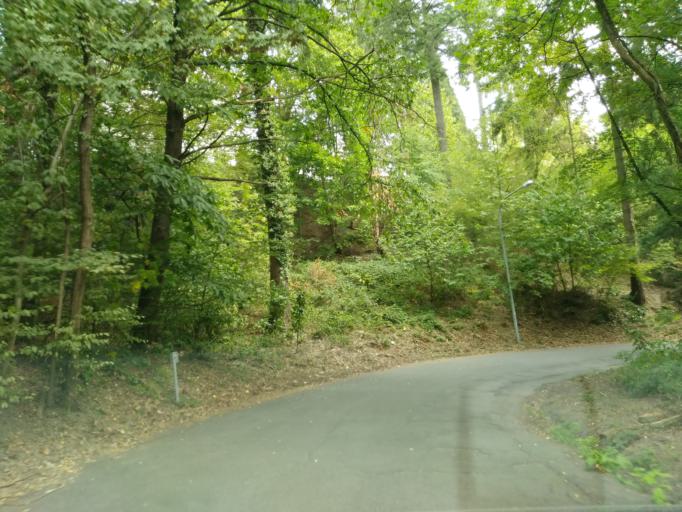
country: DE
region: North Rhine-Westphalia
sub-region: Regierungsbezirk Koln
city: Bad Honnef
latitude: 50.6501
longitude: 7.2387
